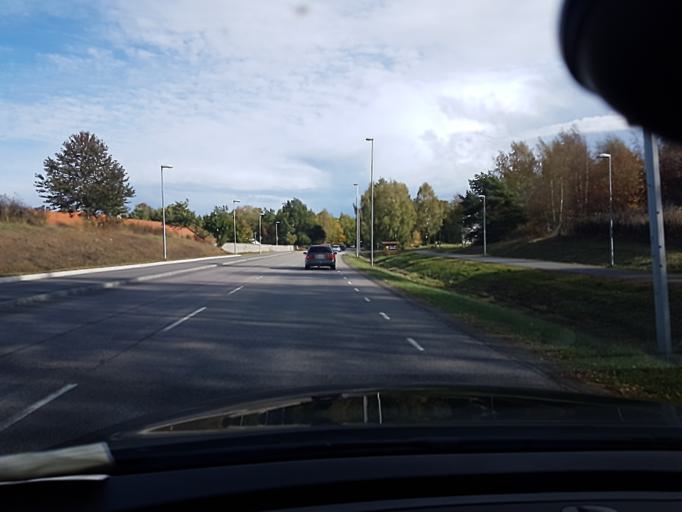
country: SE
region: Kronoberg
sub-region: Vaxjo Kommun
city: Vaexjoe
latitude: 56.8637
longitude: 14.7993
